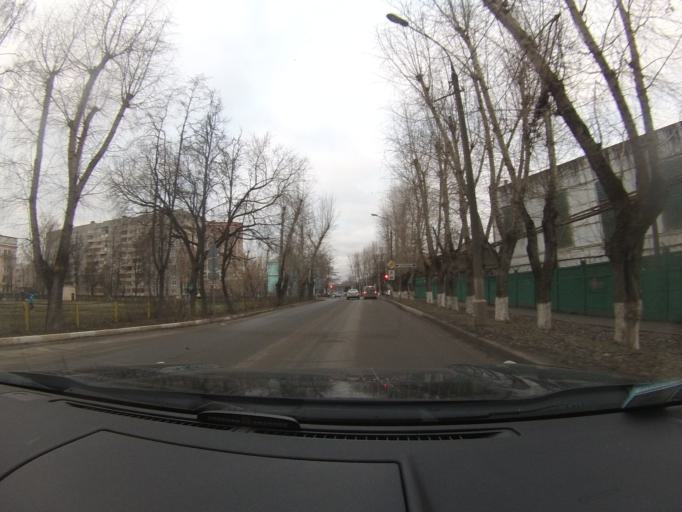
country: RU
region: Moskovskaya
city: Voskresensk
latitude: 55.3230
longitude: 38.6853
